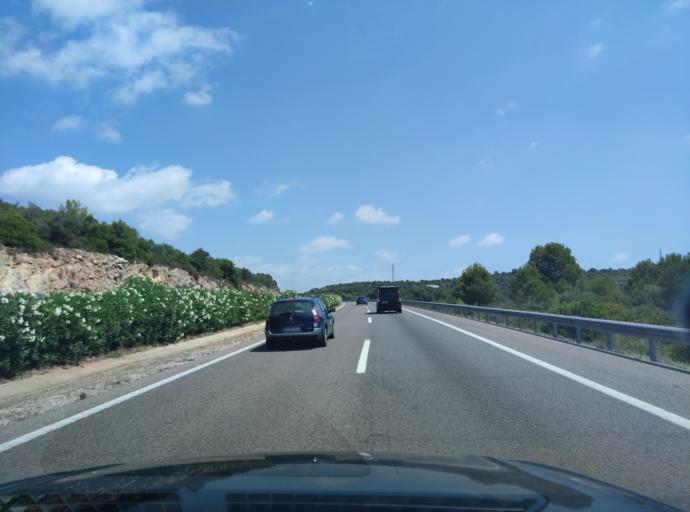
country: ES
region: Catalonia
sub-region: Provincia de Tarragona
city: Masdenverge
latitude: 40.6774
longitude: 0.5212
